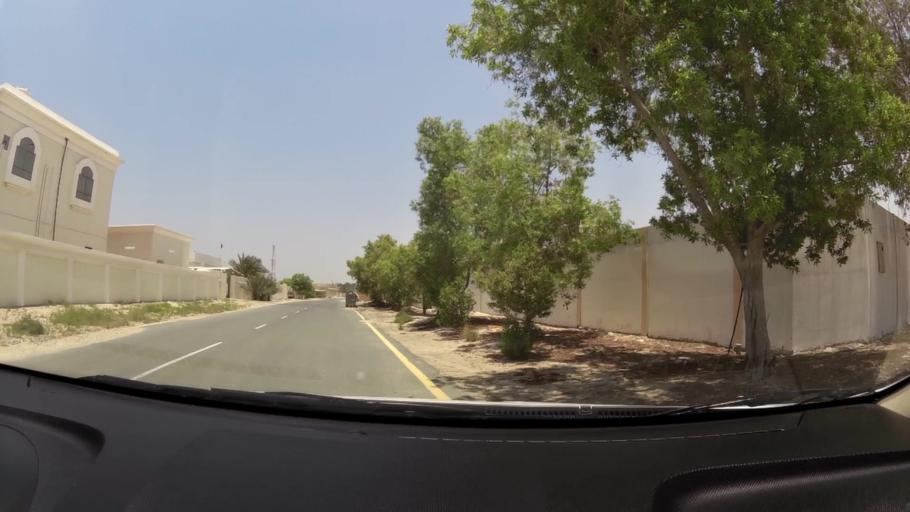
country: AE
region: Umm al Qaywayn
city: Umm al Qaywayn
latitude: 25.5333
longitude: 55.5402
